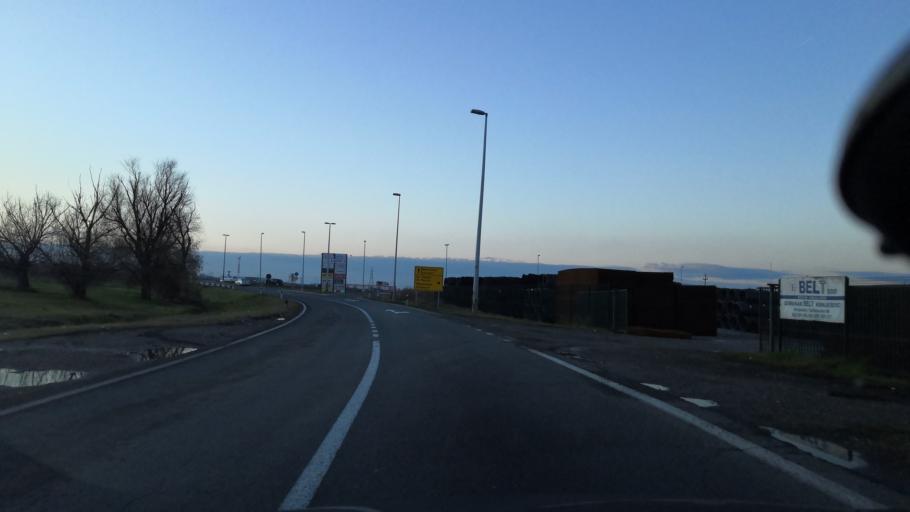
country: RS
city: Simanovci
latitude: 44.8770
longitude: 20.1292
